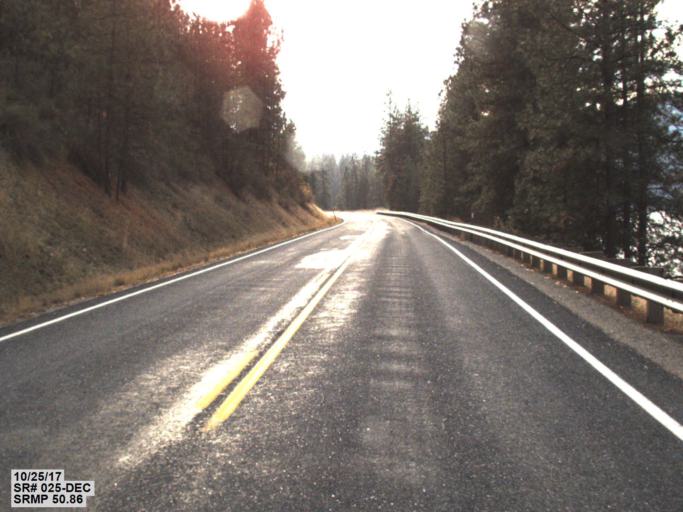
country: US
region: Washington
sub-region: Stevens County
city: Kettle Falls
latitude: 48.2199
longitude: -118.1726
